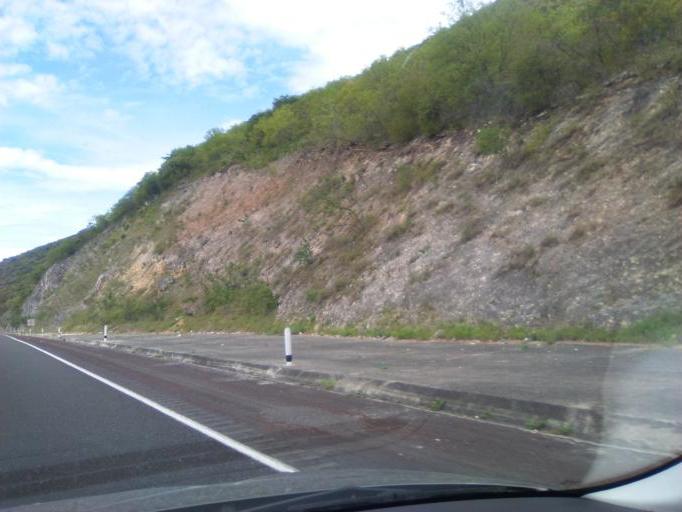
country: MX
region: Guerrero
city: Huitziltepec
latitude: 17.7780
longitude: -99.4816
